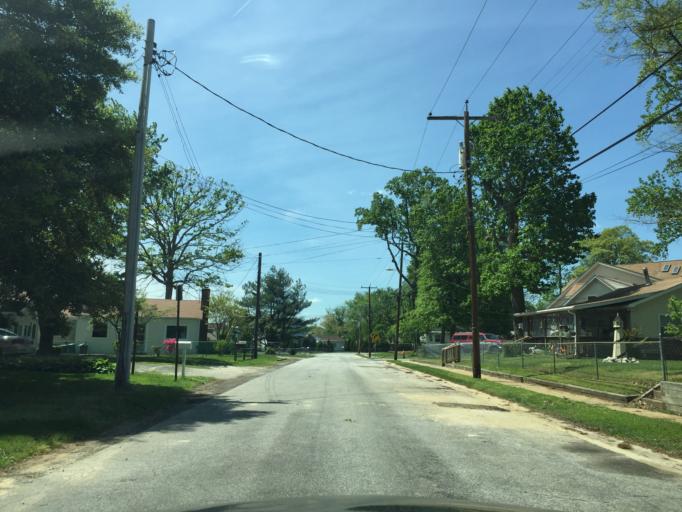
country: US
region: Maryland
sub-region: Baltimore County
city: Middle River
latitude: 39.3156
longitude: -76.4193
